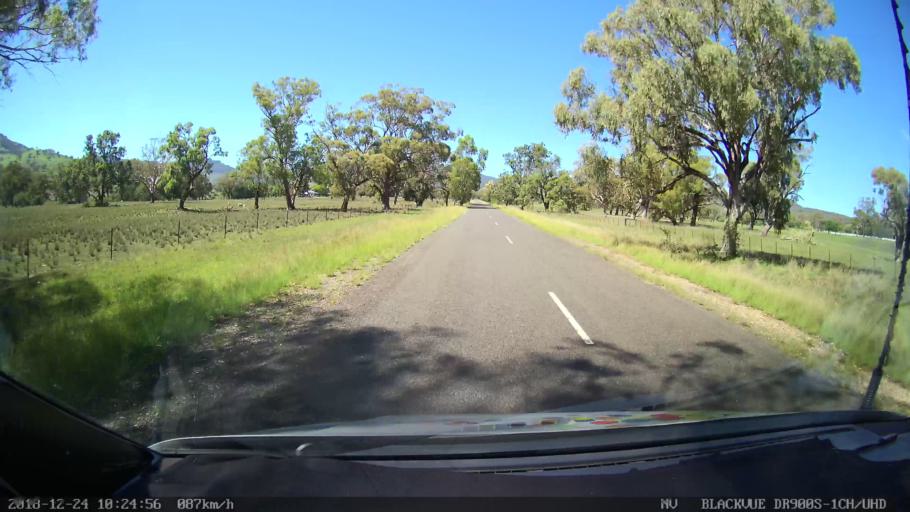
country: AU
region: New South Wales
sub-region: Liverpool Plains
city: Quirindi
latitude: -31.7927
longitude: 150.5306
